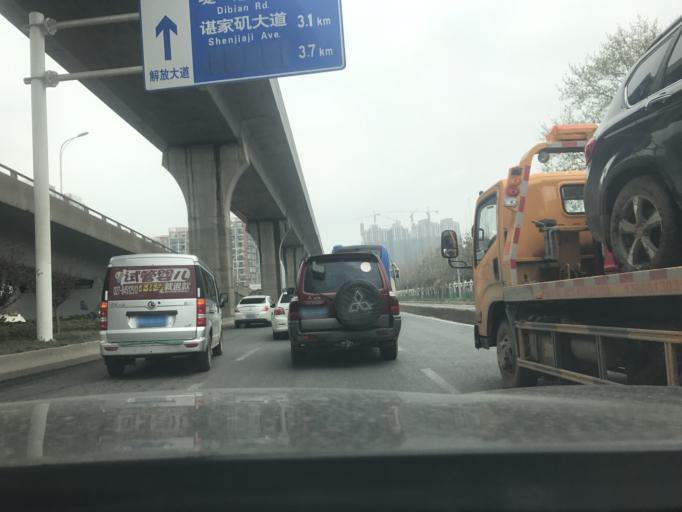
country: CN
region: Hubei
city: Houhu
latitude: 30.6612
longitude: 114.3302
